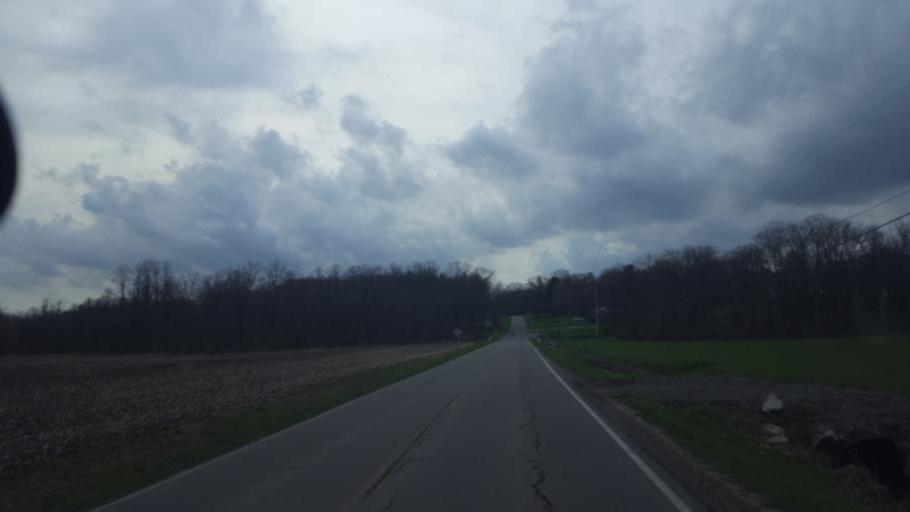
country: US
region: Ohio
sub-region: Richland County
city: Lexington
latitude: 40.6959
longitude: -82.5632
